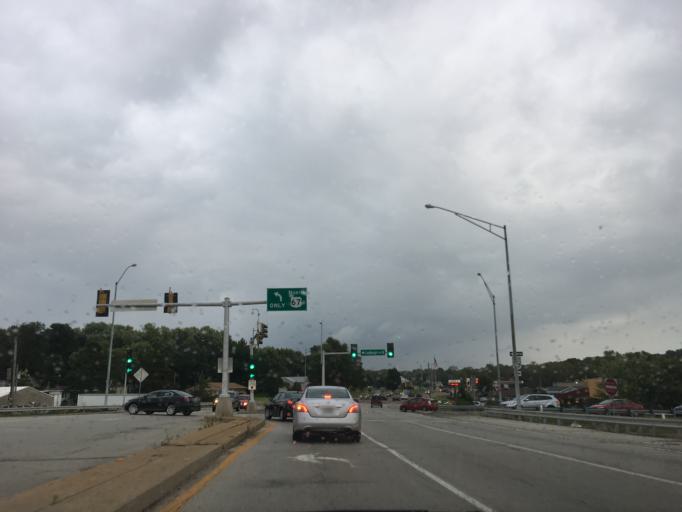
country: US
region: Missouri
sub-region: Saint Louis County
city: Maryland Heights
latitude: 38.7075
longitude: -90.4093
